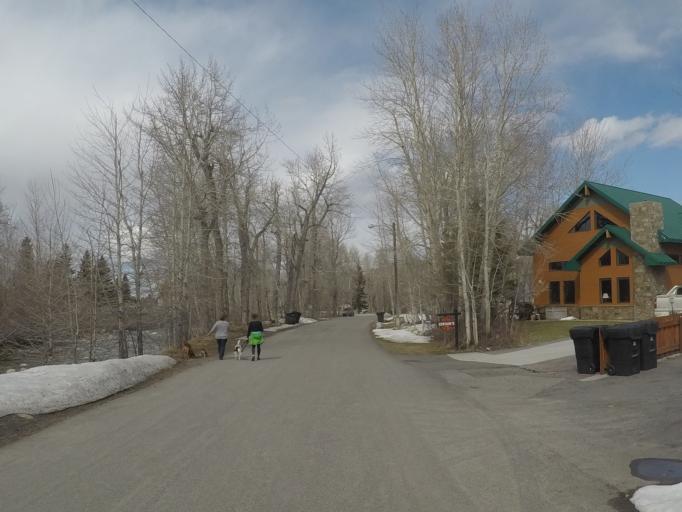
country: US
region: Montana
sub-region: Carbon County
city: Red Lodge
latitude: 45.1775
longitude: -109.2472
